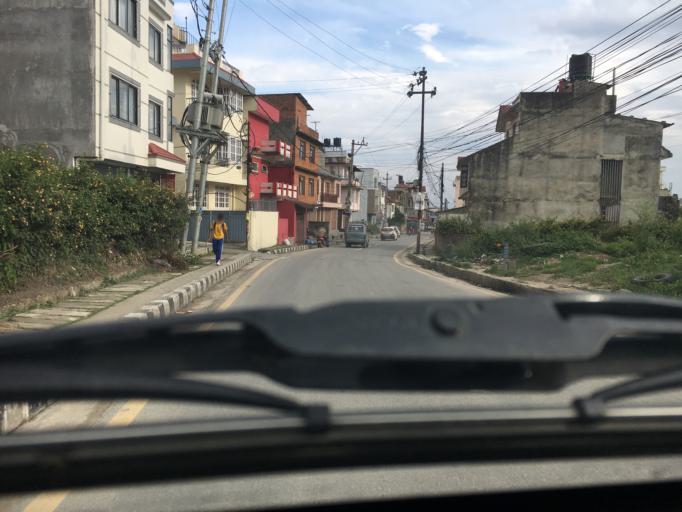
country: NP
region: Central Region
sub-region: Bagmati Zone
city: Kathmandu
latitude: 27.7444
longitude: 85.3474
